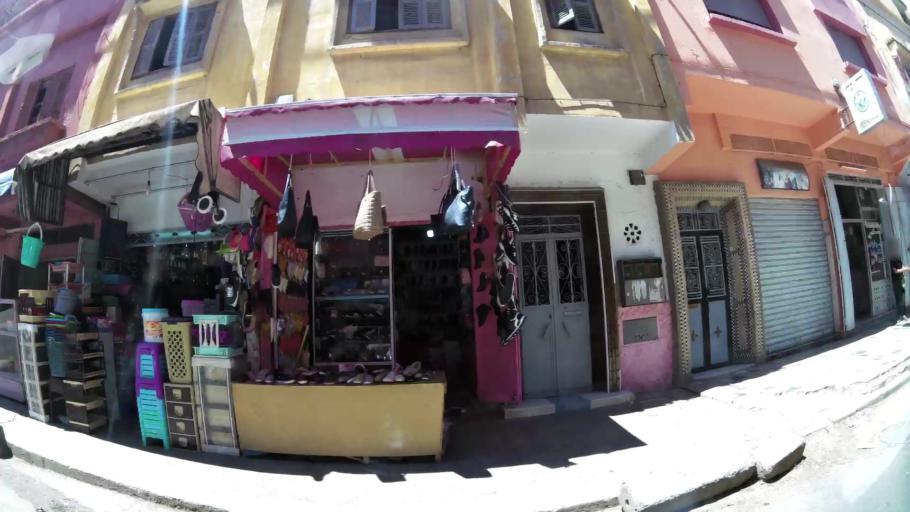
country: MA
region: Meknes-Tafilalet
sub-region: Meknes
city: Meknes
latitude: 33.9034
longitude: -5.5779
